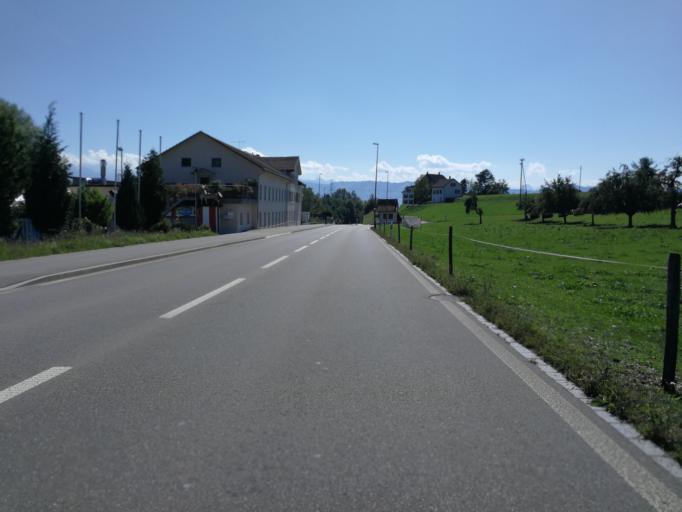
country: CH
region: Zurich
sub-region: Bezirk Hinwil
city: Hinwil
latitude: 47.2879
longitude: 8.8437
